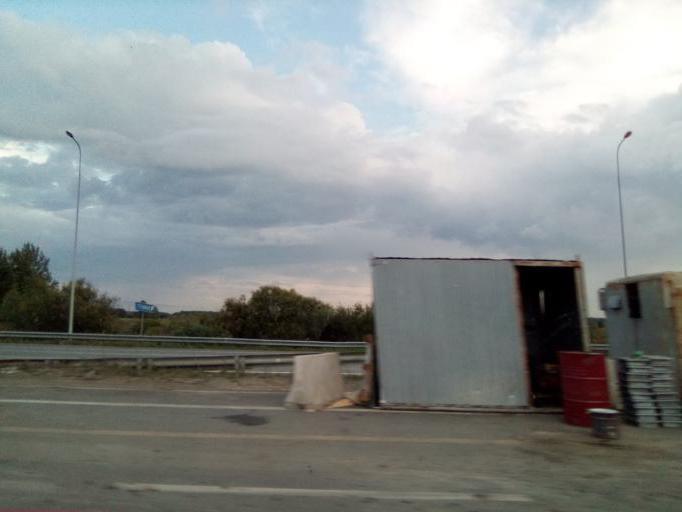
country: RU
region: Chelyabinsk
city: Poletayevo
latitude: 55.0037
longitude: 61.1566
